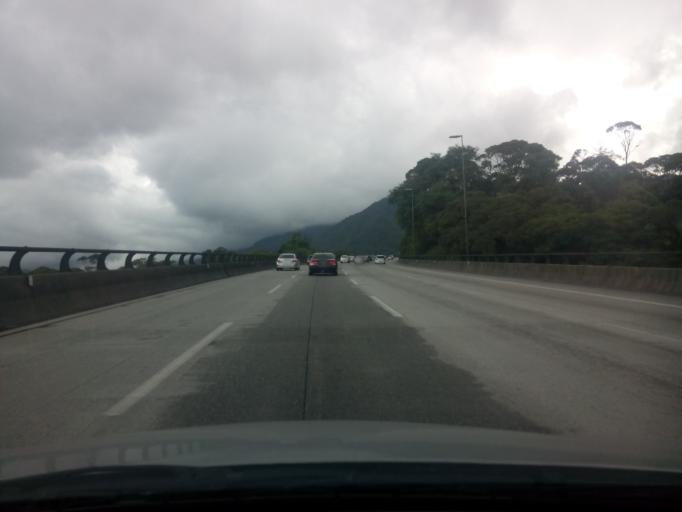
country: BR
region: Sao Paulo
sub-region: Cubatao
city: Cubatao
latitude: -23.8998
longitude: -46.4768
